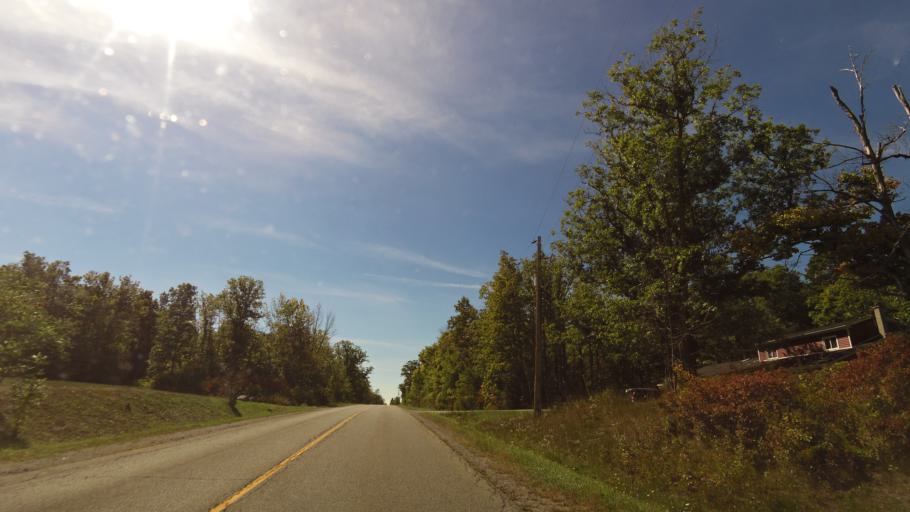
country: CA
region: Ontario
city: Ancaster
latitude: 43.0503
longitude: -80.0293
